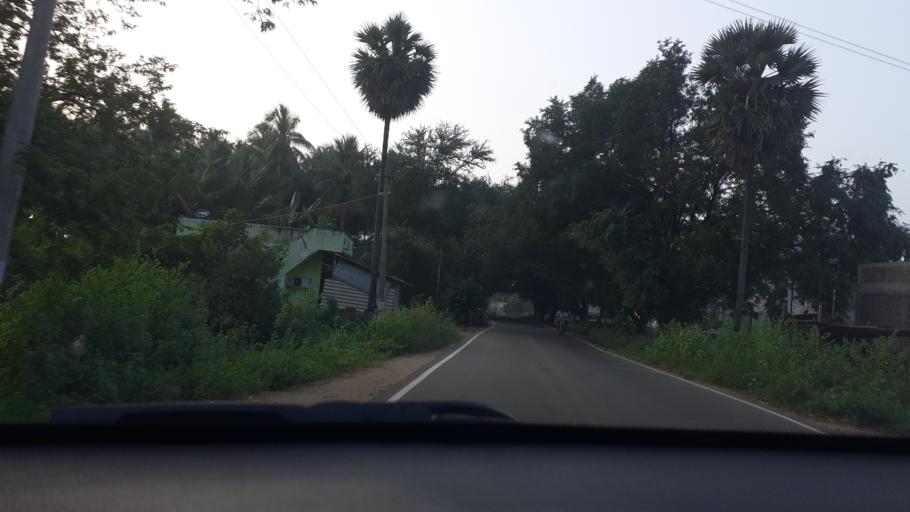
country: IN
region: Tamil Nadu
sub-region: Dindigul
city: Palani
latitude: 10.4299
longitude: 77.5259
